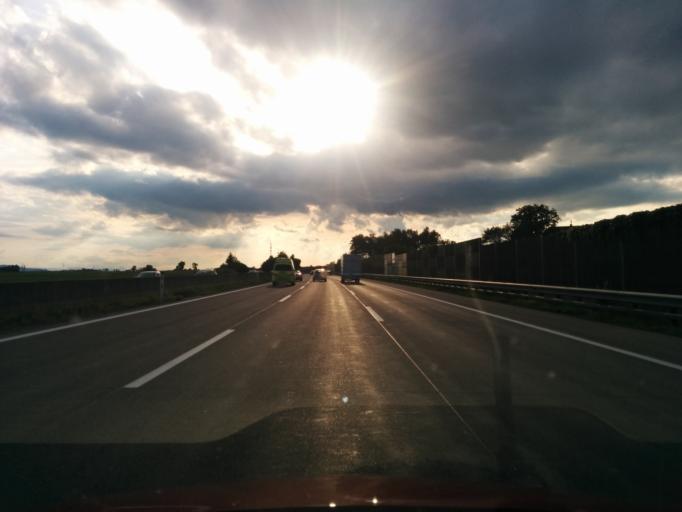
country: AT
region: Lower Austria
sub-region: Politischer Bezirk Amstetten
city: Zeillern
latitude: 48.1214
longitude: 14.7569
